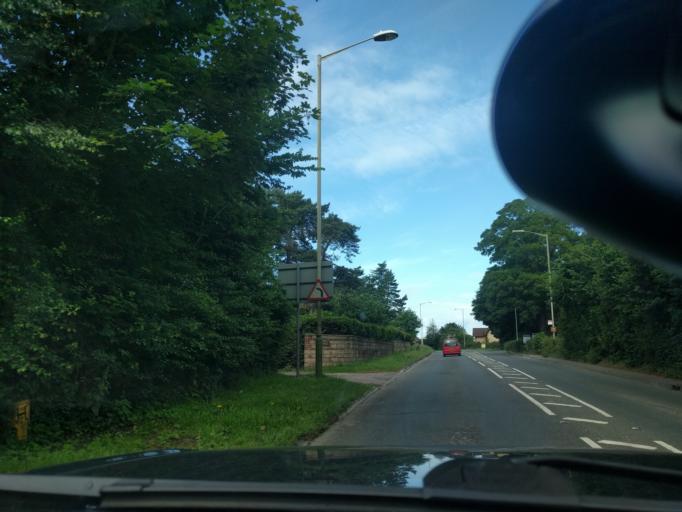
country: GB
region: England
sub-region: Wiltshire
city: Calne
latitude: 51.4396
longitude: -2.0195
